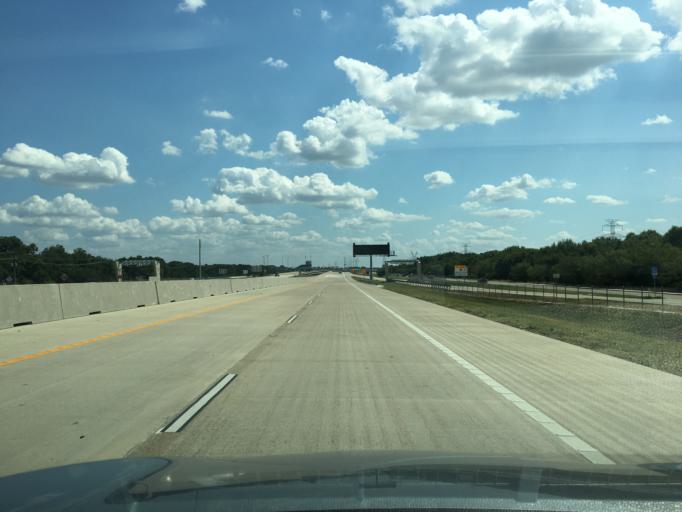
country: US
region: Texas
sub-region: Tarrant County
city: Mansfield
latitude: 32.5947
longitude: -97.0779
